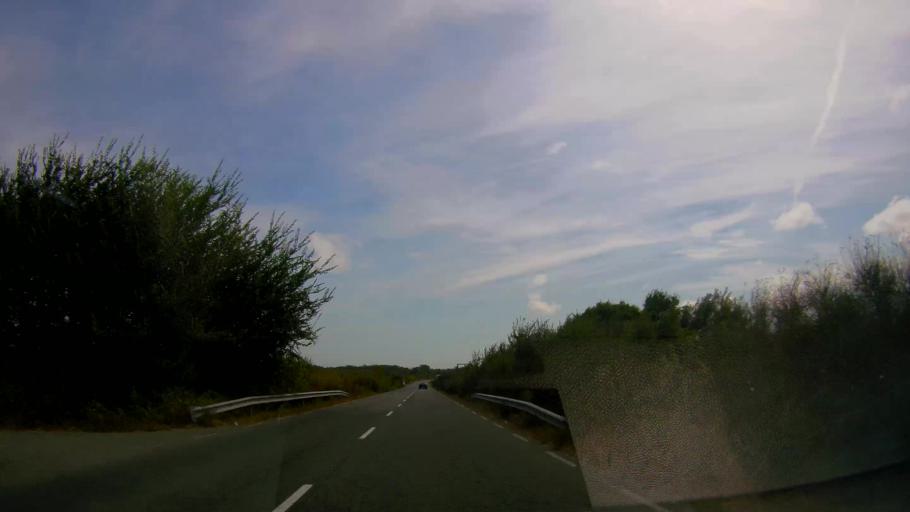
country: BG
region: Burgas
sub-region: Obshtina Sozopol
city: Sozopol
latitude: 42.3654
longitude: 27.6935
